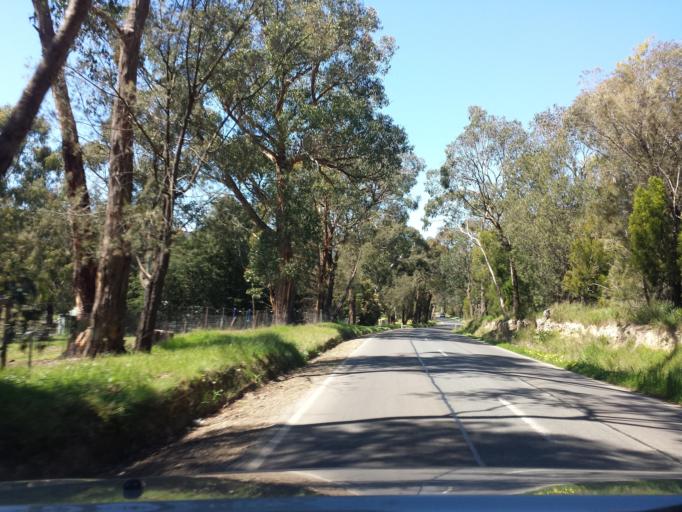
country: AU
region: Victoria
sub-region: Yarra Ranges
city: Mount Evelyn
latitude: -37.7312
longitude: 145.4414
